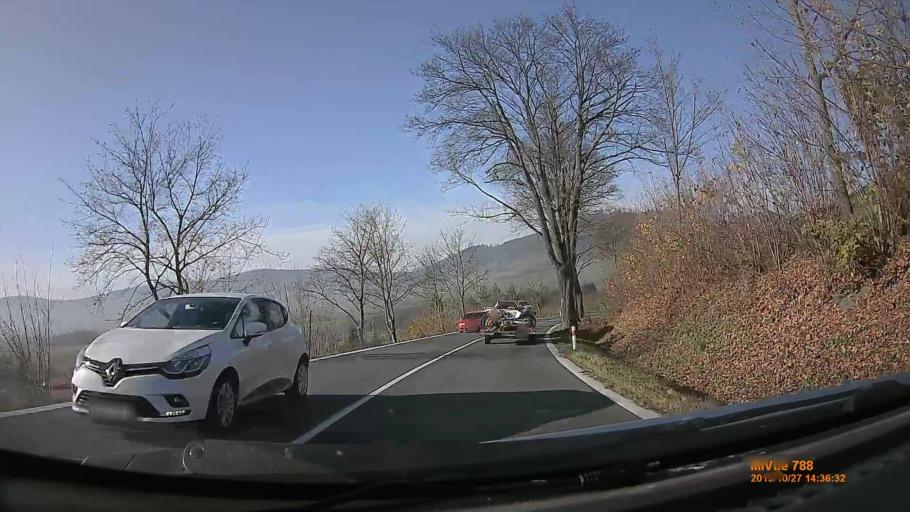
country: CZ
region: Olomoucky
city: Stity
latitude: 49.9871
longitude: 16.7932
